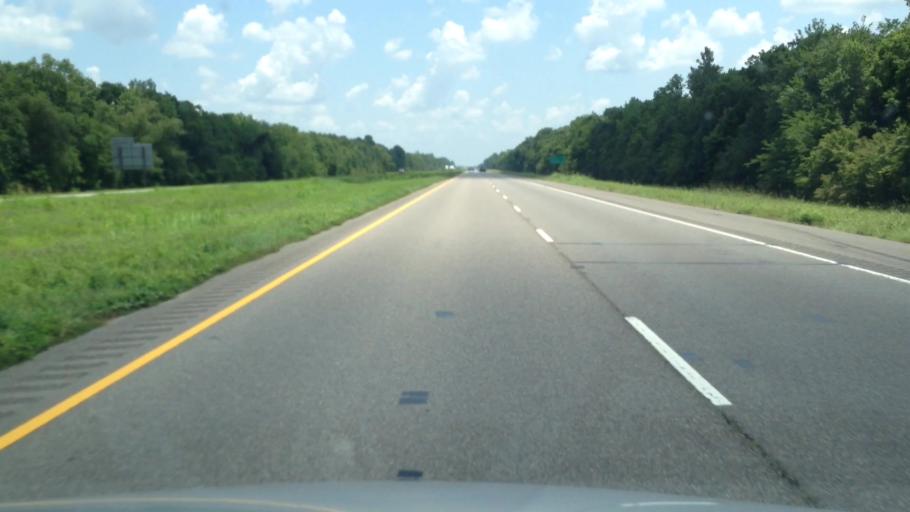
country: US
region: Louisiana
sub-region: Avoyelles Parish
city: Bunkie
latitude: 30.9779
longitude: -92.2979
